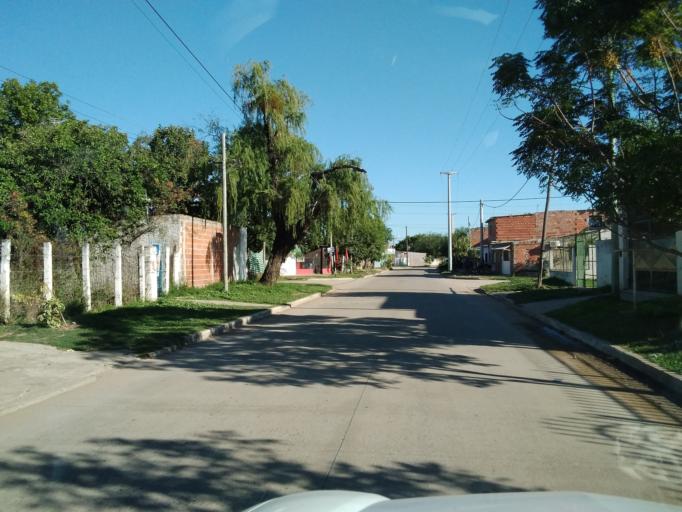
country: AR
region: Corrientes
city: Corrientes
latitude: -27.4729
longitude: -58.7917
